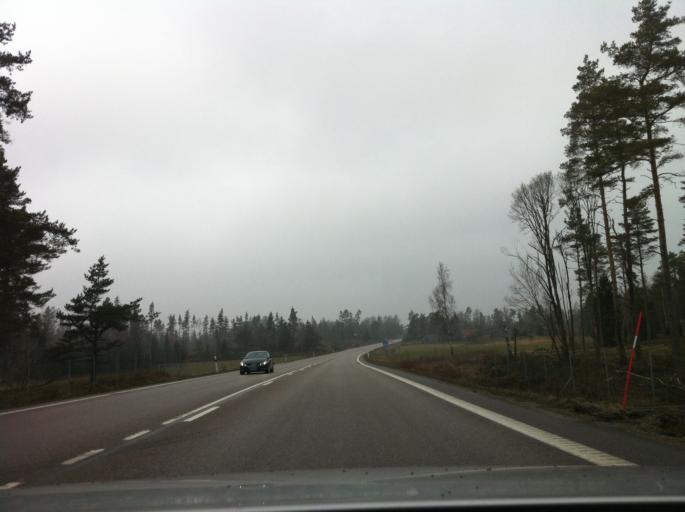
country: SE
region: Vaestra Goetaland
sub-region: Vanersborgs Kommun
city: Vanersborg
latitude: 58.4359
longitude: 12.2857
